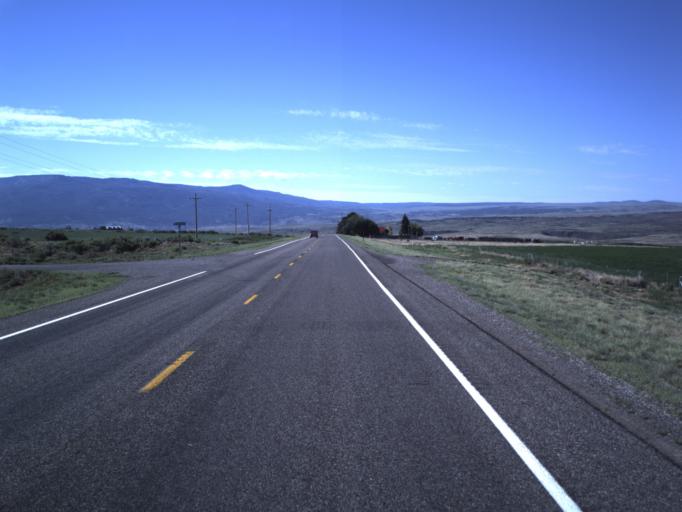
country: US
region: Utah
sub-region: Wayne County
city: Loa
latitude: 38.3792
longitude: -111.5837
